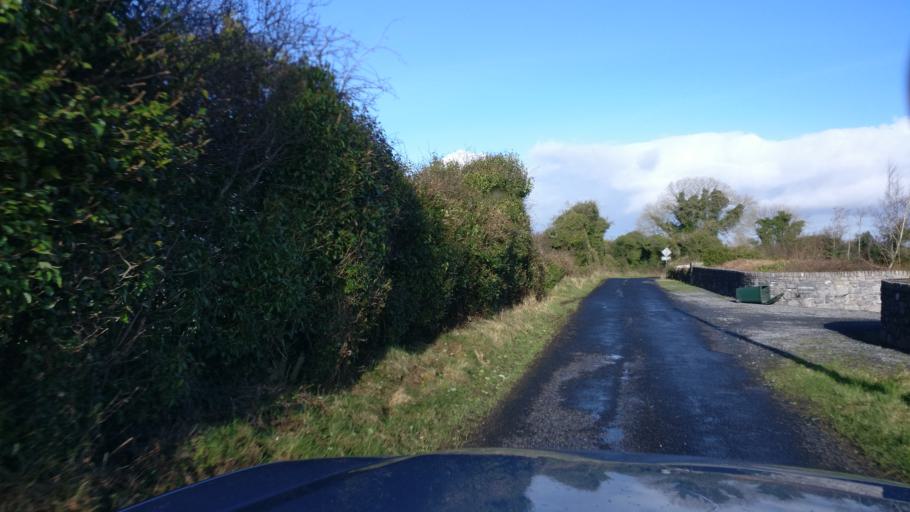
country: IE
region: Connaught
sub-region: County Galway
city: Loughrea
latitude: 53.2133
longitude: -8.6680
